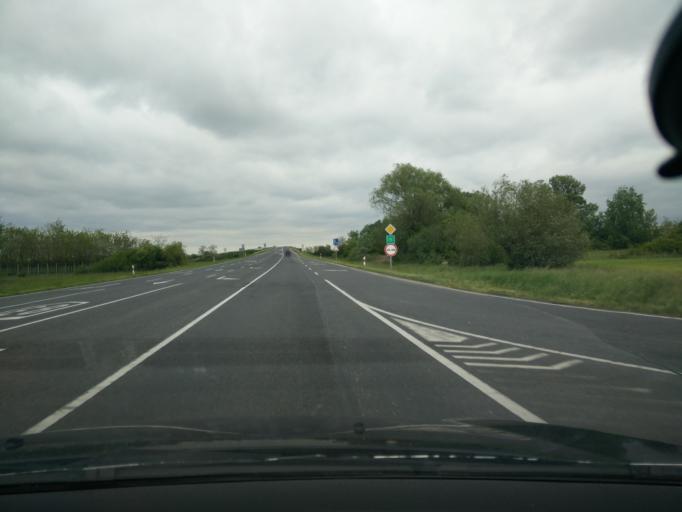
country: HU
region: Veszprem
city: Papa
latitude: 47.3403
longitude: 17.4433
